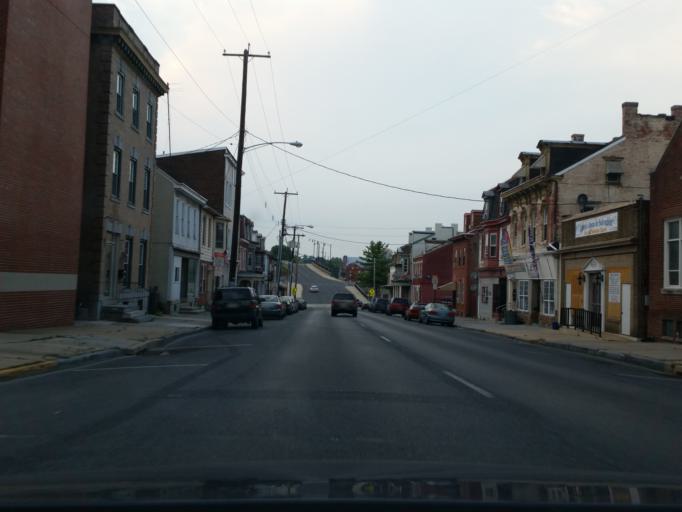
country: US
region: Pennsylvania
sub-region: Lebanon County
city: Lebanon
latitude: 40.3405
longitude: -76.4264
